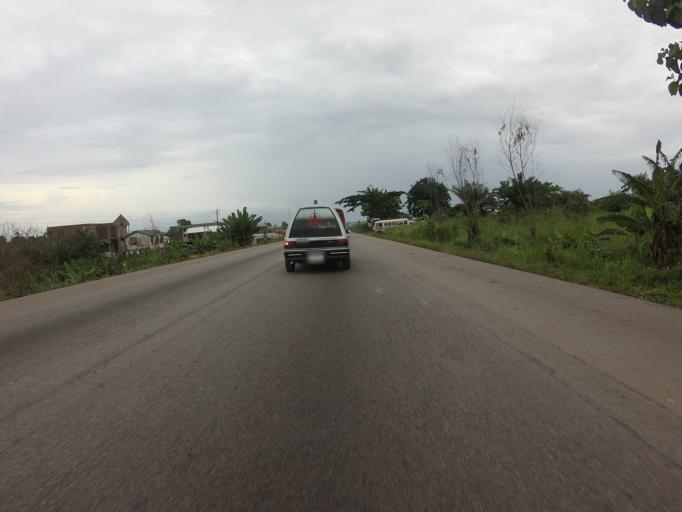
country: GH
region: Ashanti
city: Konongo
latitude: 6.6159
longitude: -1.1608
